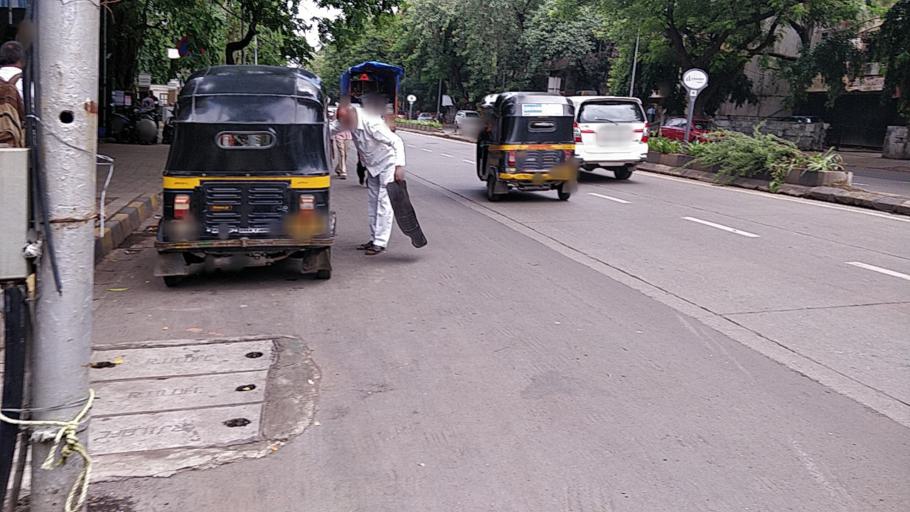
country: IN
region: Maharashtra
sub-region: Mumbai Suburban
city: Mumbai
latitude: 19.0720
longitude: 72.8340
